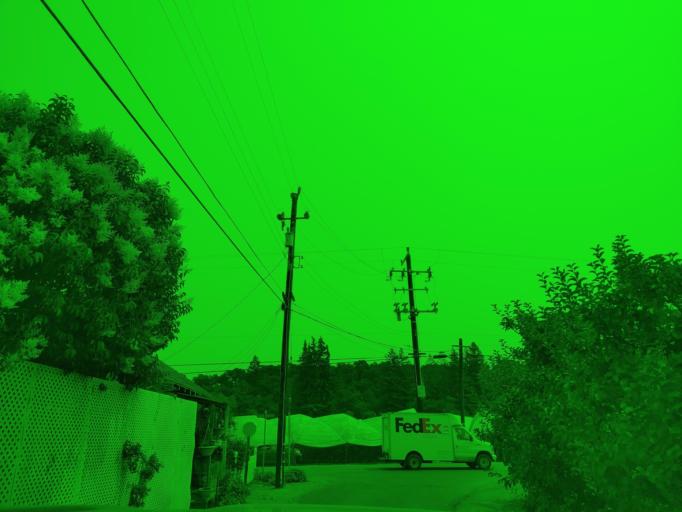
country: US
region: California
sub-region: Santa Cruz County
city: Amesti
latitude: 36.9916
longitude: -121.7767
